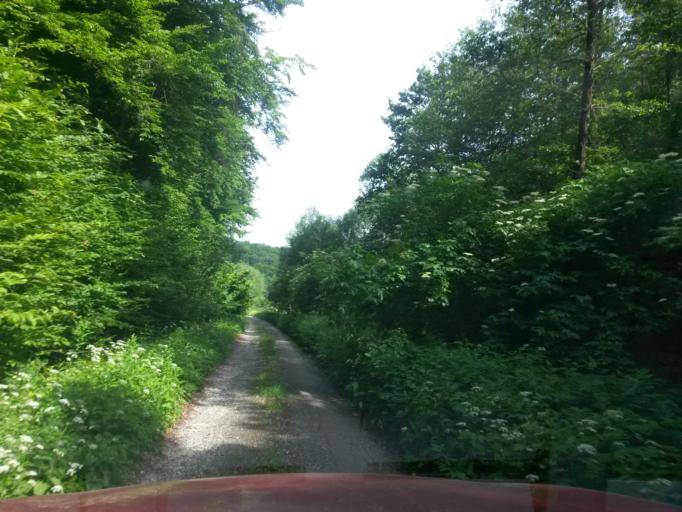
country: SK
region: Kosicky
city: Kosice
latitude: 48.7381
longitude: 21.1148
